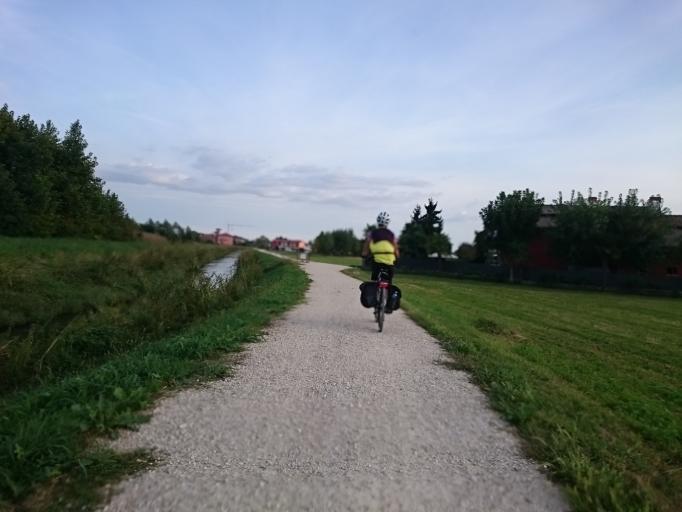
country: IT
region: Veneto
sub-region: Provincia di Vicenza
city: Camisano Vicentino
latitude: 45.5267
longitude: 11.7022
